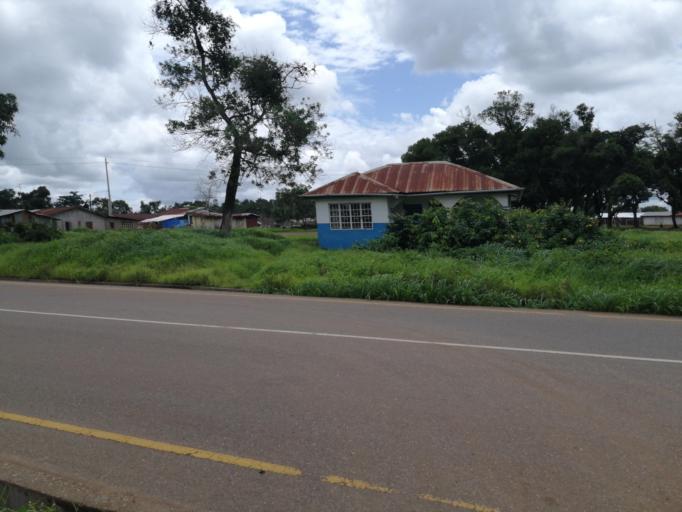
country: SL
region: Northern Province
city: Port Loko
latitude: 8.7741
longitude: -12.7863
